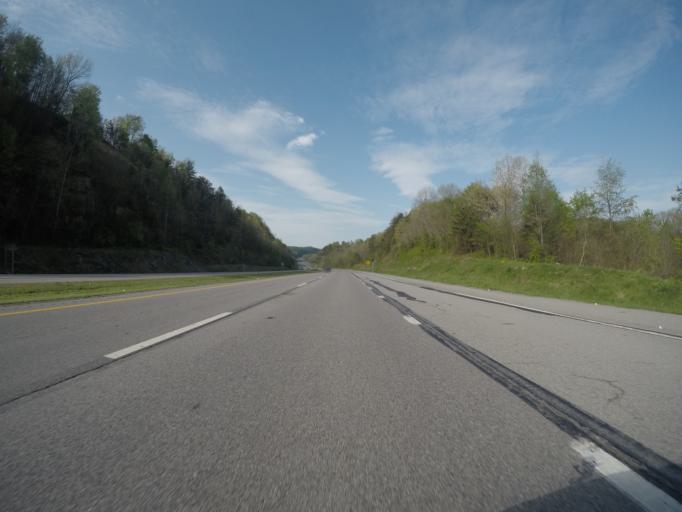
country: US
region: West Virginia
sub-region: Kanawha County
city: Dunbar
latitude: 38.3154
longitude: -81.7248
